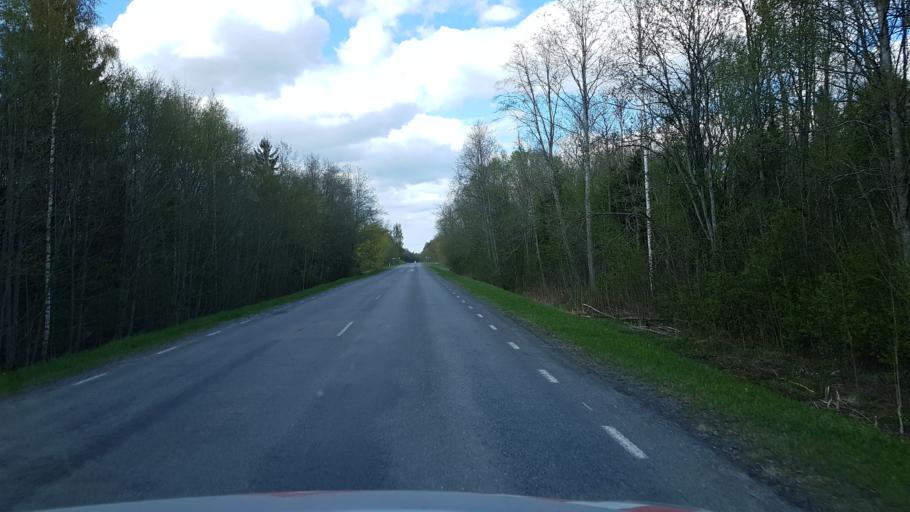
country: EE
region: Harju
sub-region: Keila linn
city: Keila
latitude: 59.2534
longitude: 24.4557
